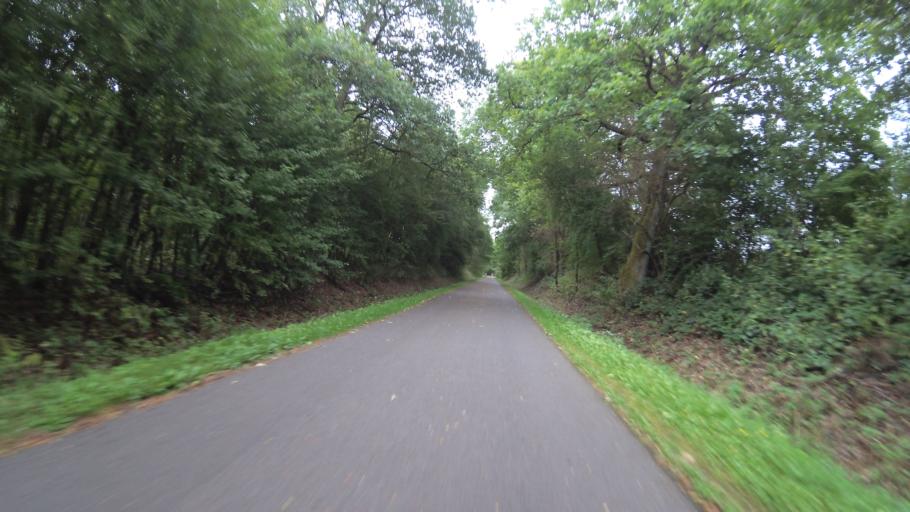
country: DE
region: Saarland
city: Sankt Wendel
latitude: 49.4819
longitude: 7.1583
